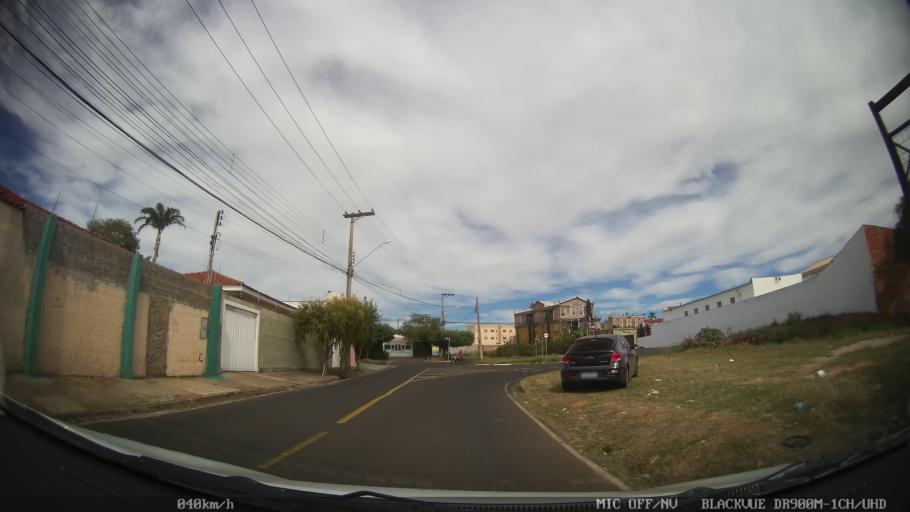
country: BR
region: Sao Paulo
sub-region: Catanduva
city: Catanduva
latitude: -21.1448
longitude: -48.9619
